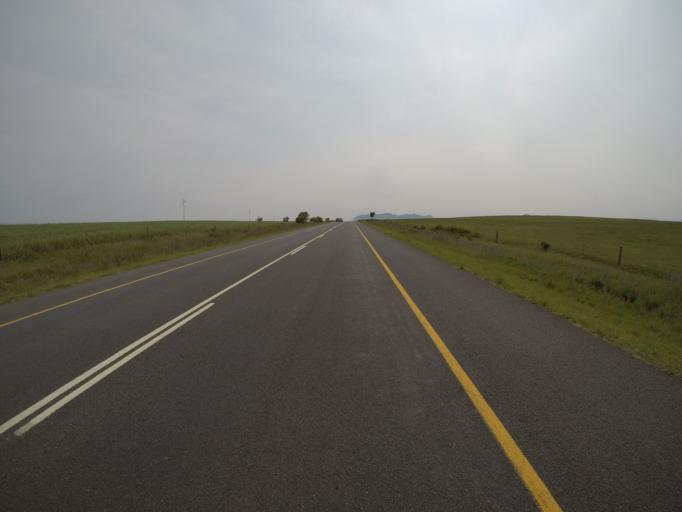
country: ZA
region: Western Cape
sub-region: West Coast District Municipality
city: Malmesbury
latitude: -33.5227
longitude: 18.8468
